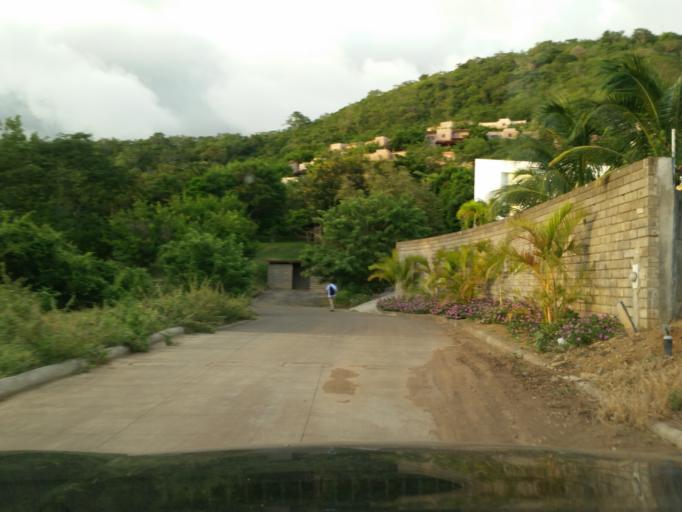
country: NI
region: Rivas
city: San Juan del Sur
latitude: 11.2669
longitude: -85.8586
